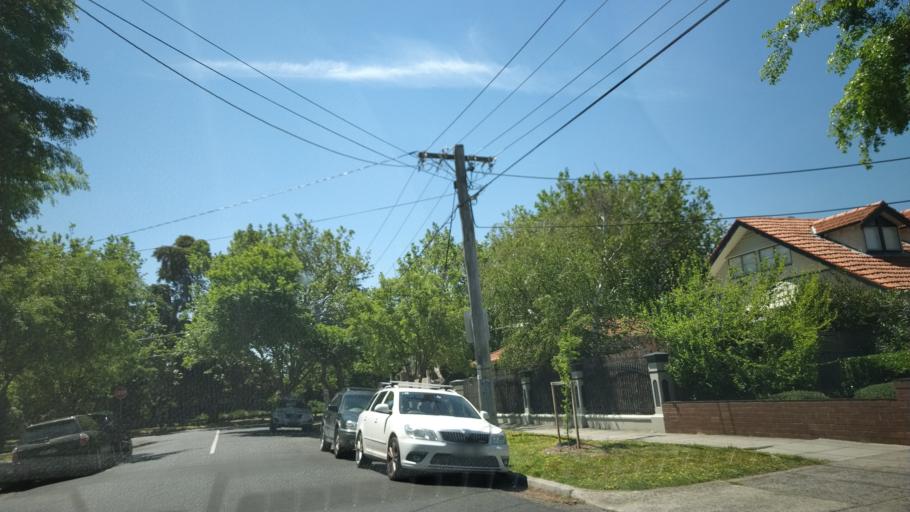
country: AU
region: Victoria
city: Ormond
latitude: -37.8983
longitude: 145.0423
